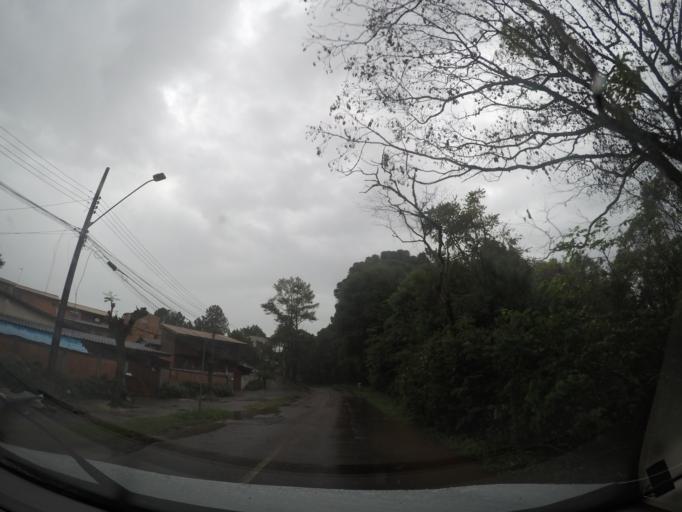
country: BR
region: Parana
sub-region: Curitiba
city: Curitiba
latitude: -25.4523
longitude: -49.3766
